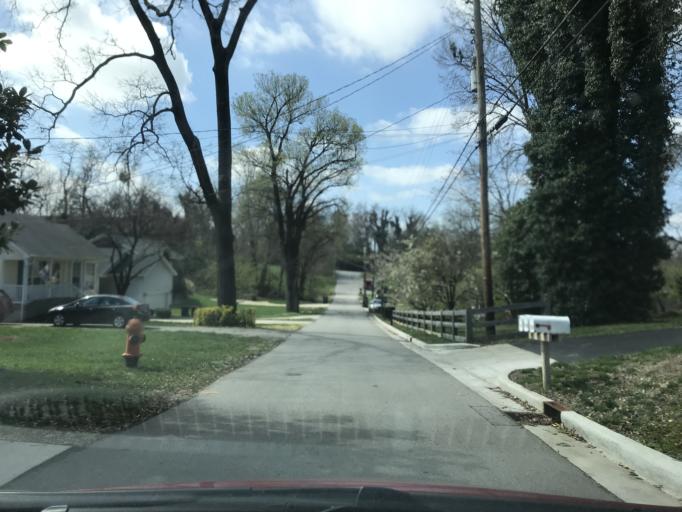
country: US
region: Kentucky
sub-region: Jefferson County
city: Audubon Park
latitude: 38.2074
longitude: -85.7120
